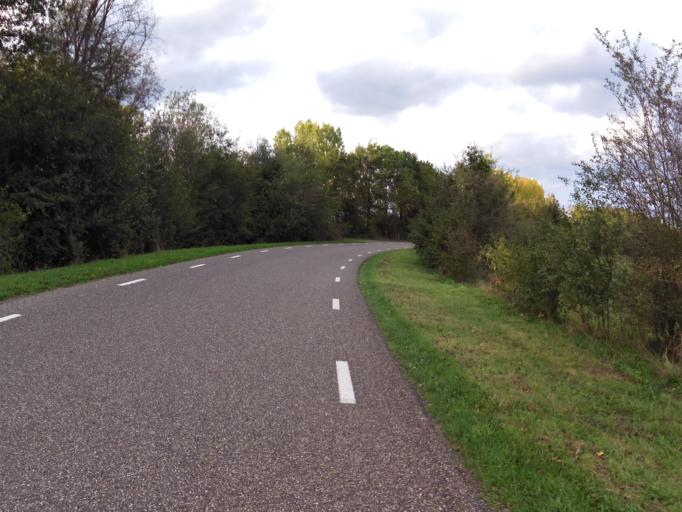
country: NL
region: Limburg
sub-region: Gemeente Maasgouw
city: Maasbracht
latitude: 51.1807
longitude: 5.9249
